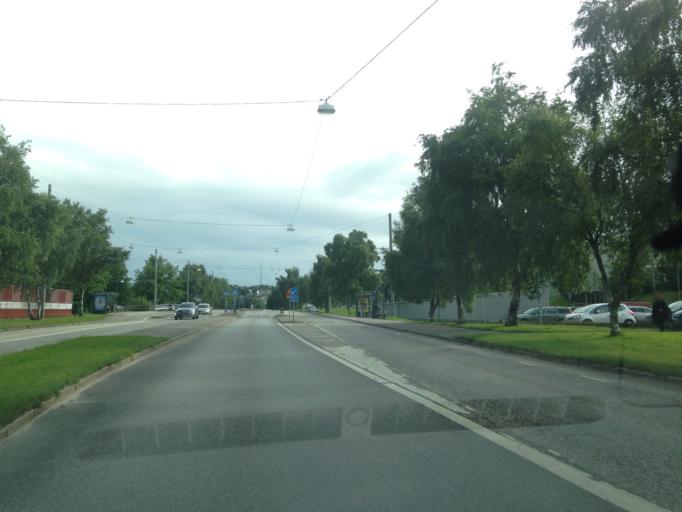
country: SE
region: Vaestra Goetaland
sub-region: Goteborg
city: Goeteborg
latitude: 57.7466
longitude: 11.9780
